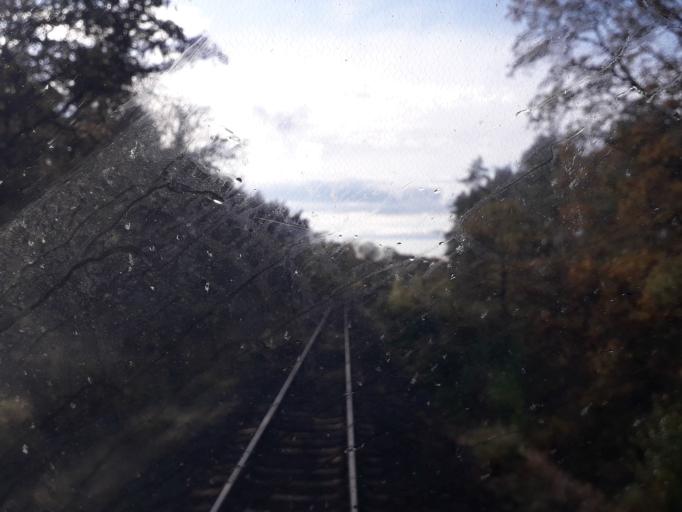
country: DE
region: Brandenburg
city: Gross Pankow
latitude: 53.1284
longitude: 12.0751
